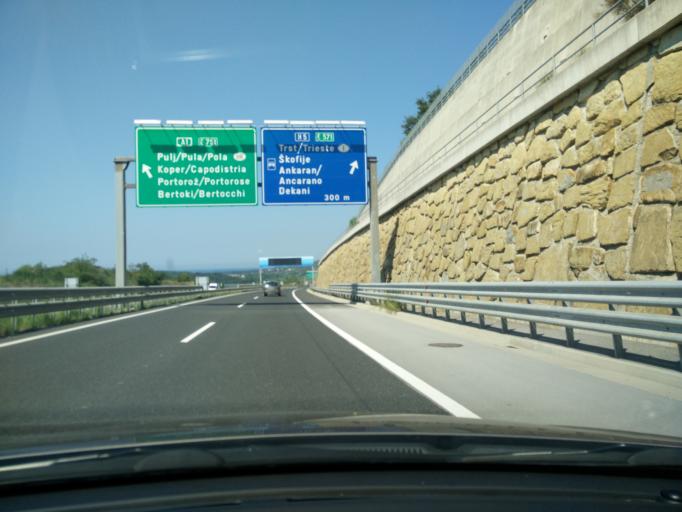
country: SI
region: Koper-Capodistria
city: Dekani
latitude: 45.5558
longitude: 13.7983
